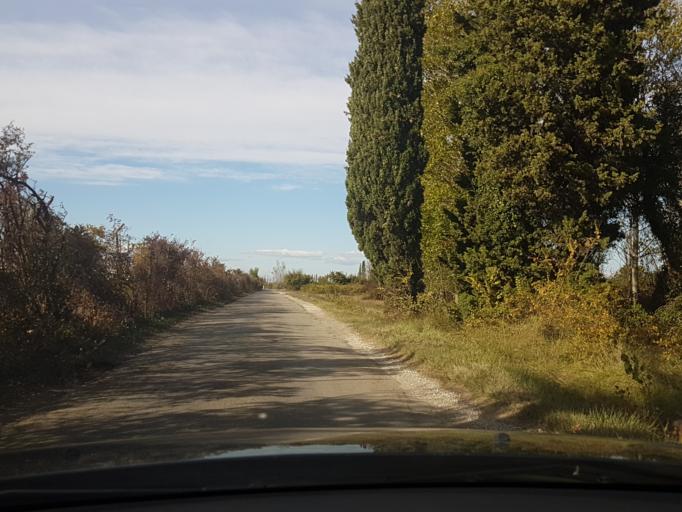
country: FR
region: Provence-Alpes-Cote d'Azur
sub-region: Departement du Vaucluse
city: Saint-Saturnin-les-Avignon
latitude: 43.9768
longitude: 4.9401
